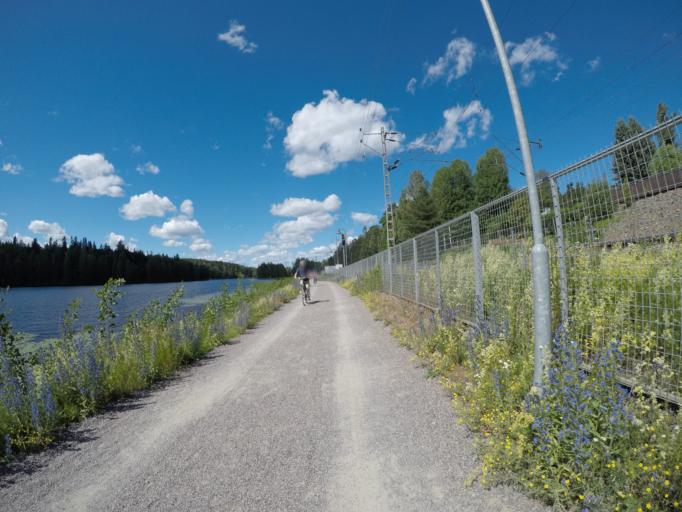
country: FI
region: Haeme
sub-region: Haemeenlinna
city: Haemeenlinna
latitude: 61.0119
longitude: 24.4596
